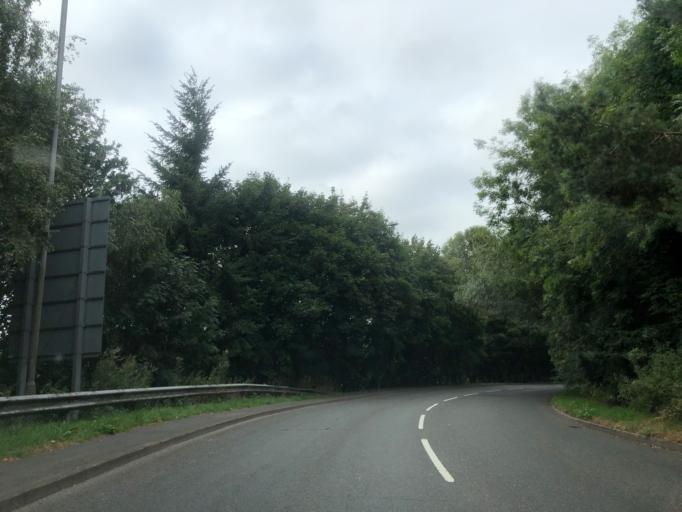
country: GB
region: England
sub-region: Warwickshire
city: Warwick
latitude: 52.2906
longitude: -1.5999
